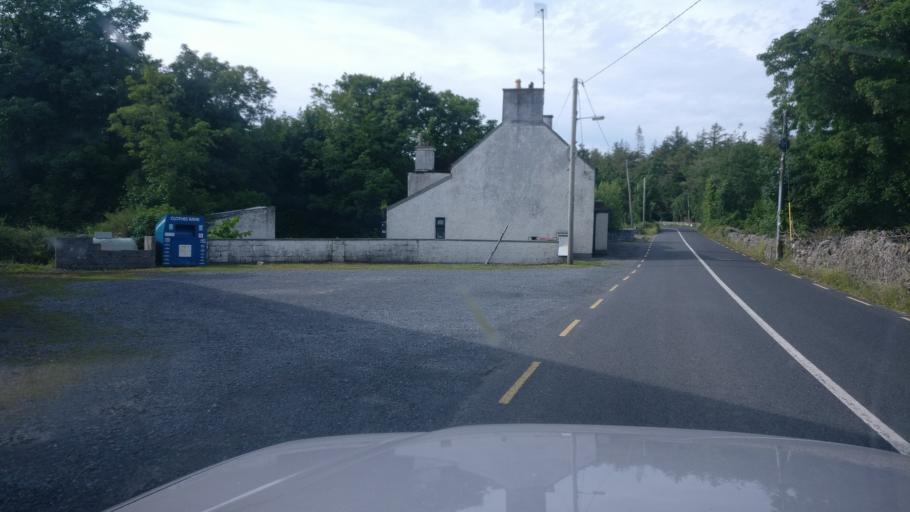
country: IE
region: Connaught
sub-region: County Galway
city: Gort
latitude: 53.1126
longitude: -8.7381
